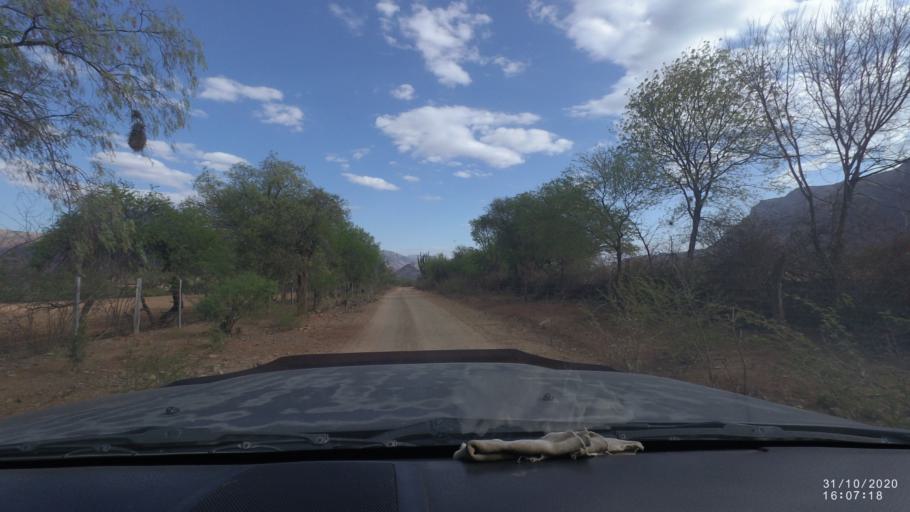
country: BO
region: Chuquisaca
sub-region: Provincia Zudanez
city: Mojocoya
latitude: -18.3790
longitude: -64.6457
